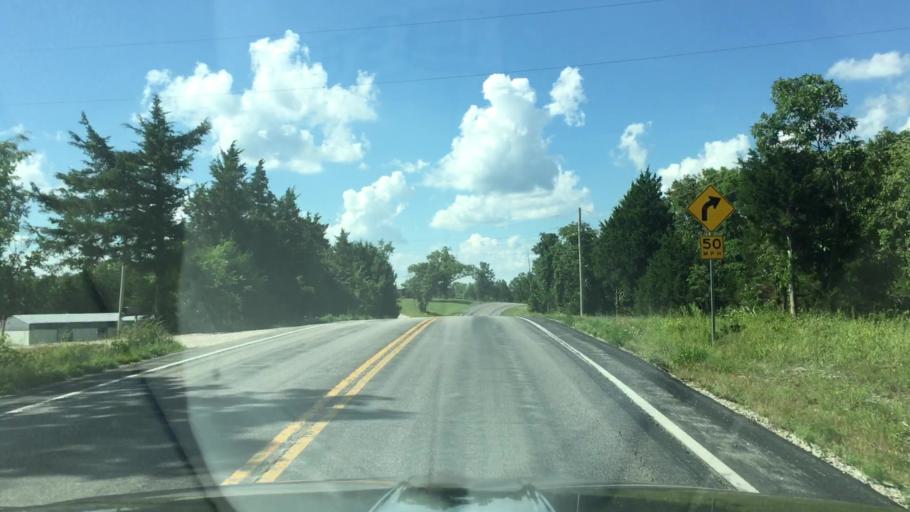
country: US
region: Missouri
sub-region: Miller County
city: Tuscumbia
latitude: 38.0908
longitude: -92.4986
